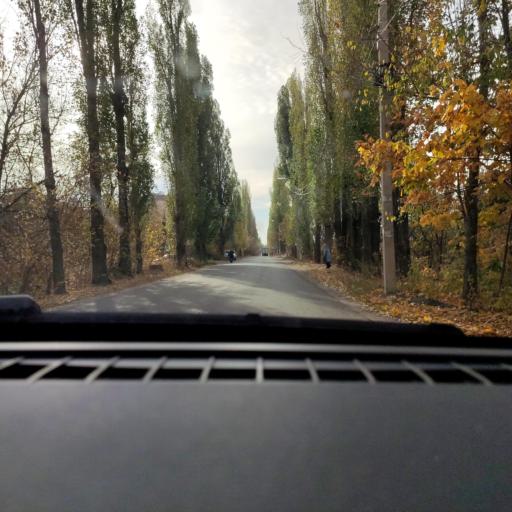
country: RU
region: Voronezj
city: Novaya Usman'
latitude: 51.6459
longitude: 39.3037
